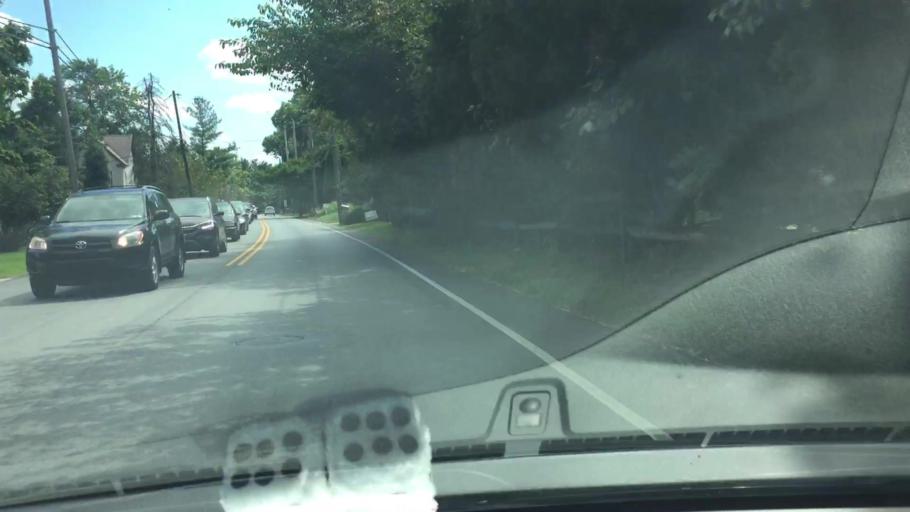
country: US
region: Pennsylvania
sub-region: Delaware County
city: Lima
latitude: 39.9087
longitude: -75.4401
